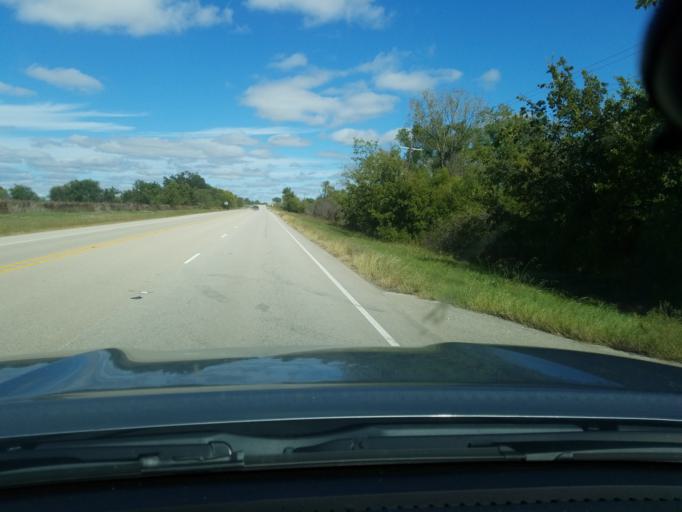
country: US
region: Texas
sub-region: Hamilton County
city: Hamilton
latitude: 31.6518
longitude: -98.1456
